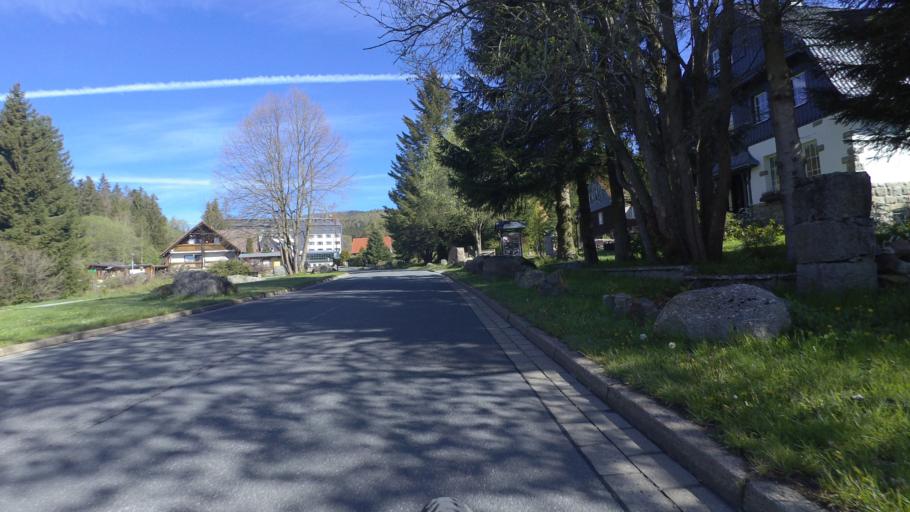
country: DE
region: Lower Saxony
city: Braunlage
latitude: 51.7687
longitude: 10.6517
